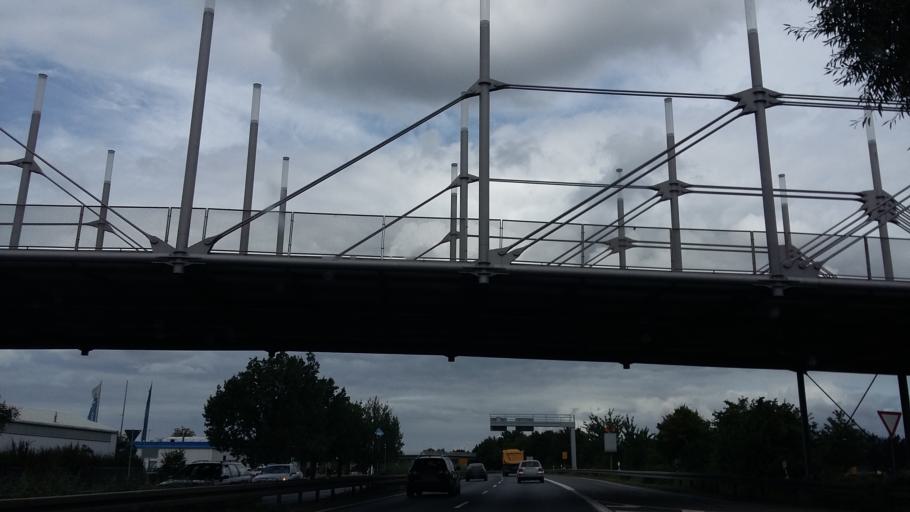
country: DE
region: Lower Saxony
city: Laatzen
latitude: 52.3283
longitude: 9.8131
